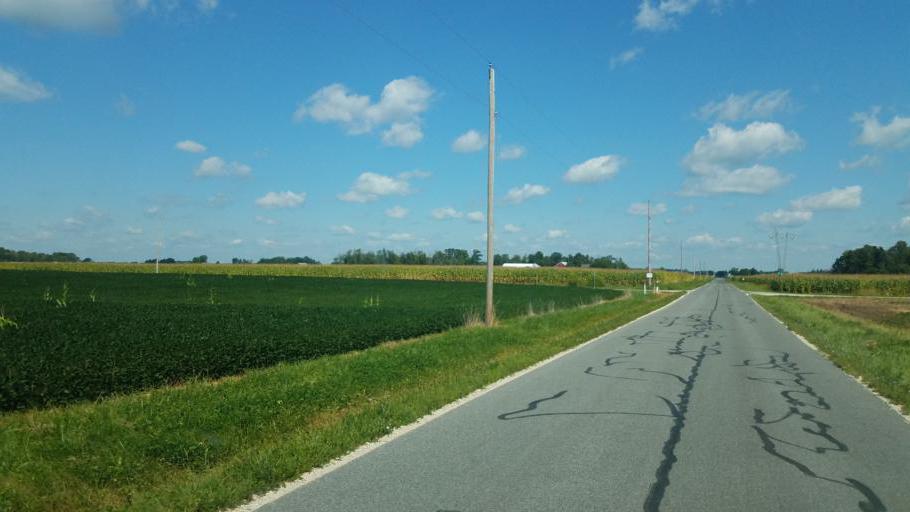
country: US
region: Ohio
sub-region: Wyandot County
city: Carey
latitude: 41.0353
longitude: -83.3245
